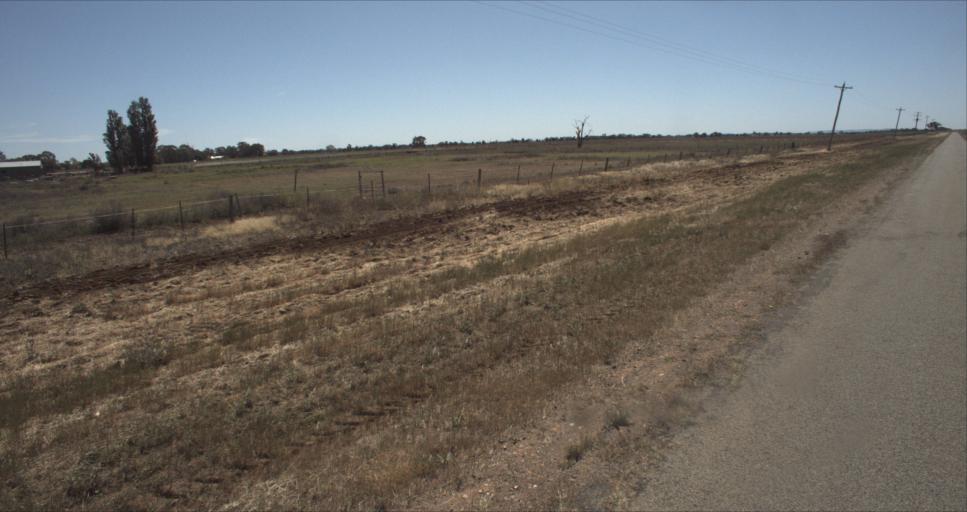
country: AU
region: New South Wales
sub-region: Leeton
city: Leeton
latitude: -34.5101
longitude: 146.3448
